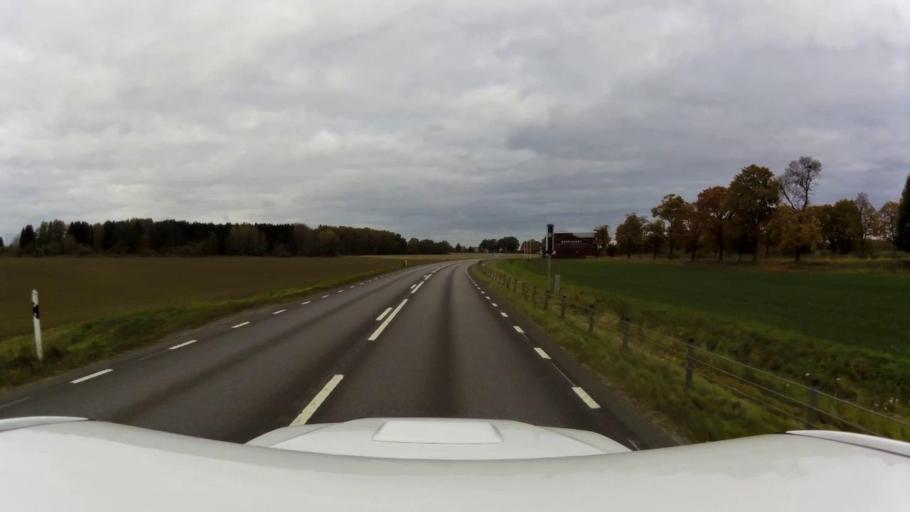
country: SE
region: OEstergoetland
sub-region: Linkopings Kommun
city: Ljungsbro
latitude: 58.5173
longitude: 15.4302
